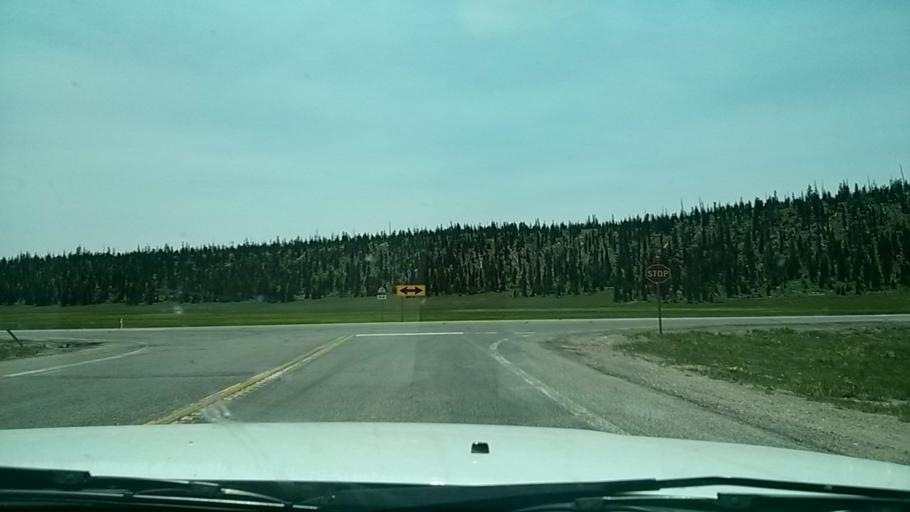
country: US
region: Utah
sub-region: Iron County
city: Cedar City
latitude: 37.5729
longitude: -112.8364
